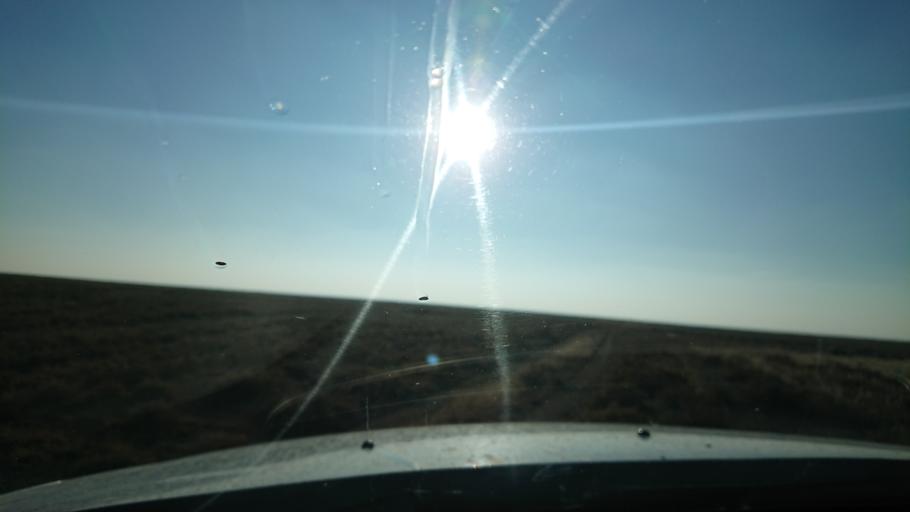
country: TR
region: Aksaray
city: Sultanhani
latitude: 38.3887
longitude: 33.5930
